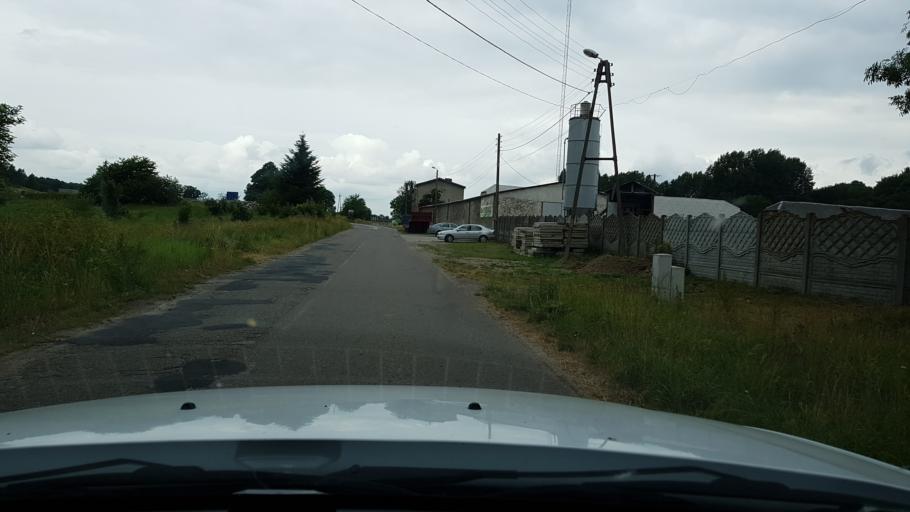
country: PL
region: West Pomeranian Voivodeship
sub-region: Powiat stargardzki
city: Insko
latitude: 53.4656
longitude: 15.5863
